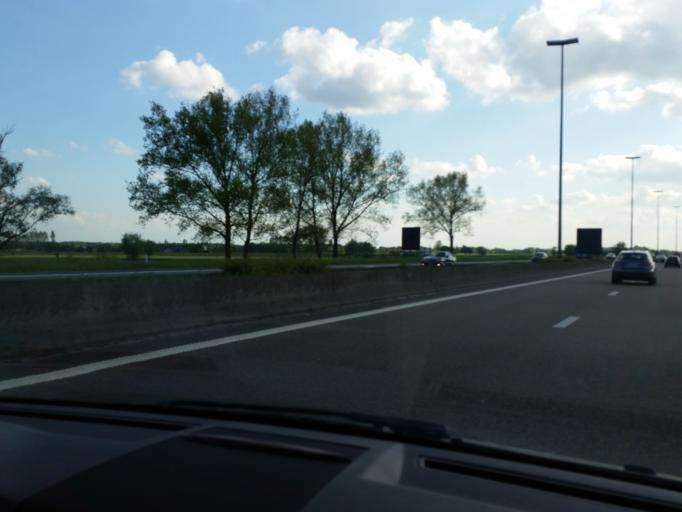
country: BE
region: Flanders
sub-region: Provincie Oost-Vlaanderen
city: Lokeren
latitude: 51.0810
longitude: 4.0095
